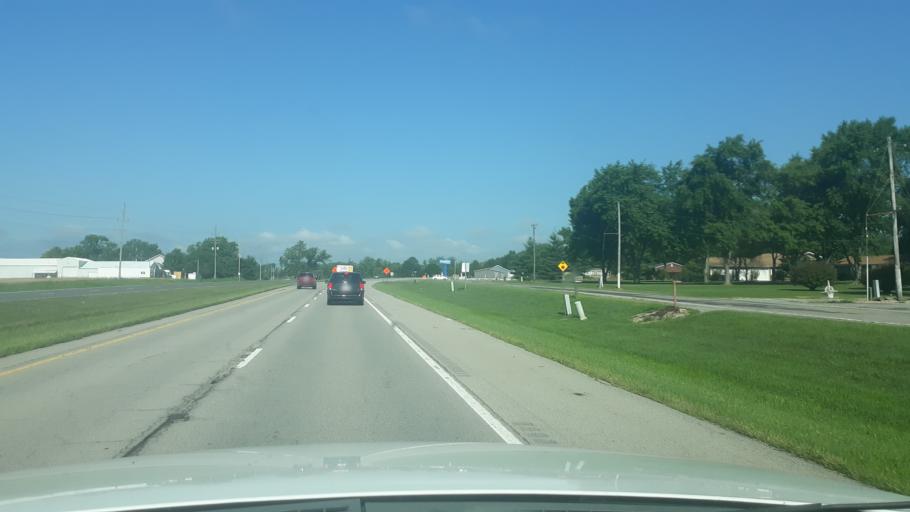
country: US
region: Illinois
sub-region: Williamson County
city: Marion
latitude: 37.7299
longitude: -88.8802
